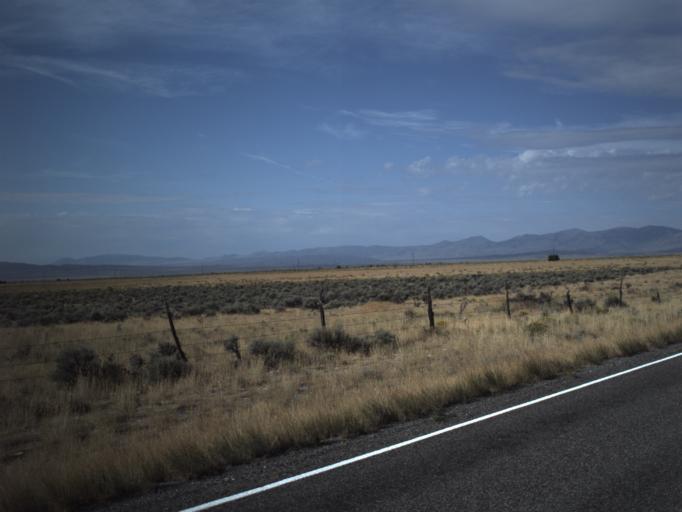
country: US
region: Idaho
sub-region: Cassia County
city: Burley
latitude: 41.8167
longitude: -113.3577
